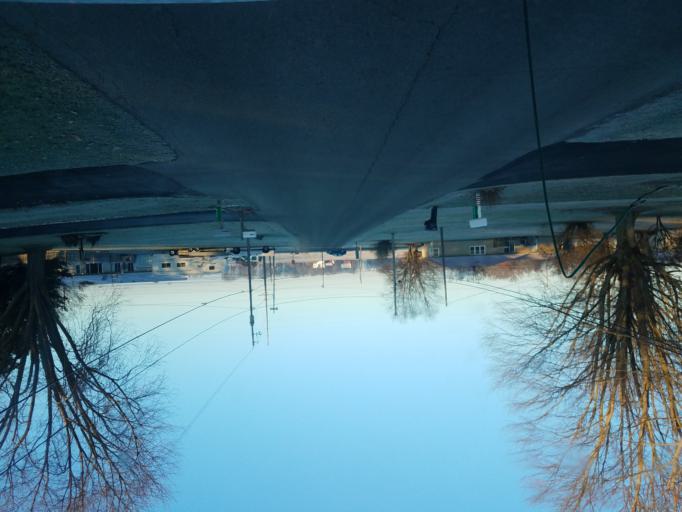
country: US
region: Ohio
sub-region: Marion County
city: Marion
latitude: 40.5630
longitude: -83.0910
